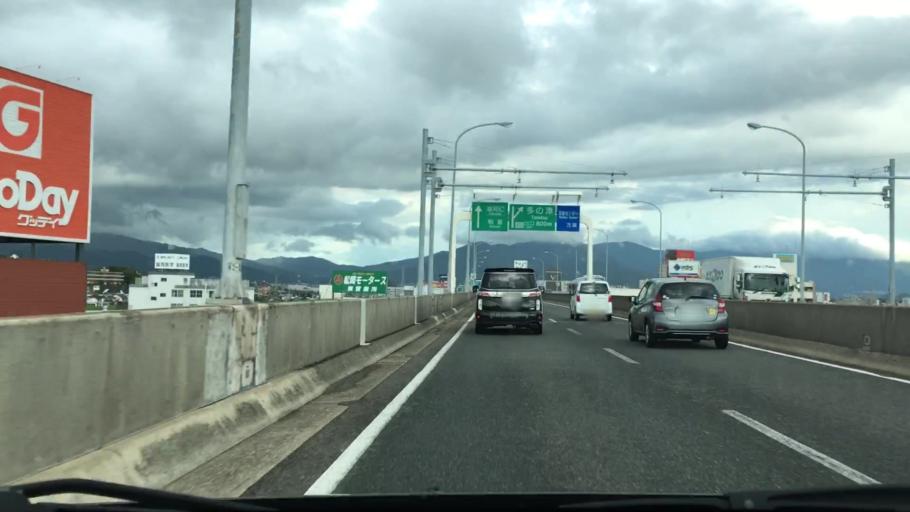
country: JP
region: Fukuoka
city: Fukuoka-shi
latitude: 33.6311
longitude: 130.4372
